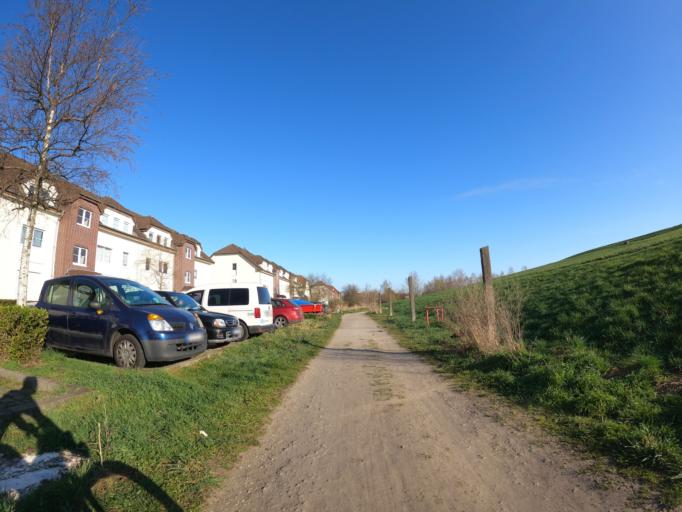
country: DE
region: Berlin
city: Gropiusstadt
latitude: 52.4101
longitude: 13.4507
